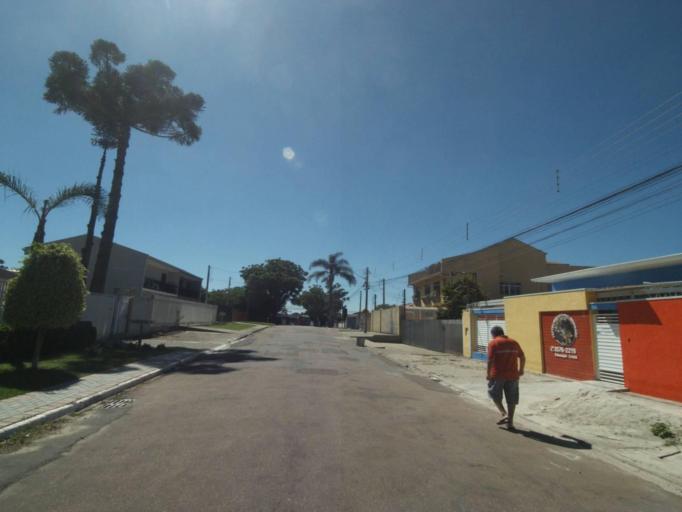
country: BR
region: Parana
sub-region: Curitiba
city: Curitiba
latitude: -25.4790
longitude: -49.3378
